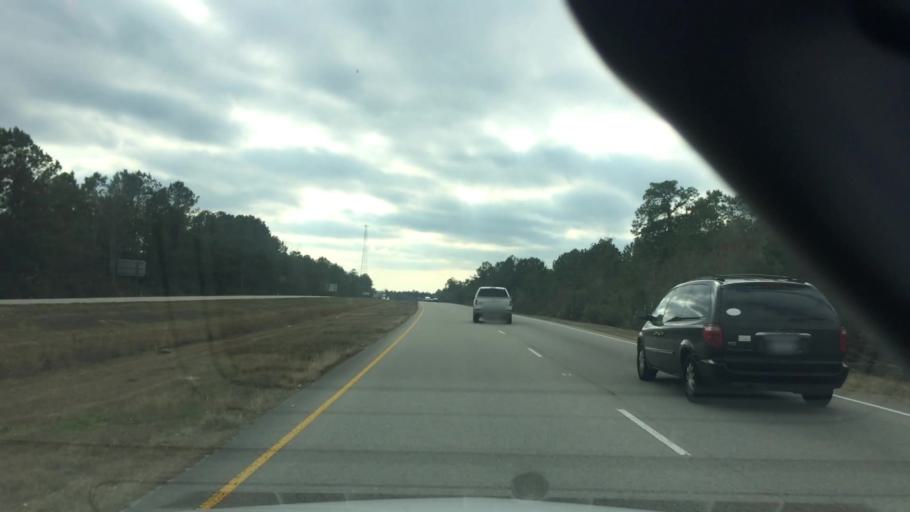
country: US
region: North Carolina
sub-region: Brunswick County
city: Shallotte
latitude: 33.9710
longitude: -78.4110
